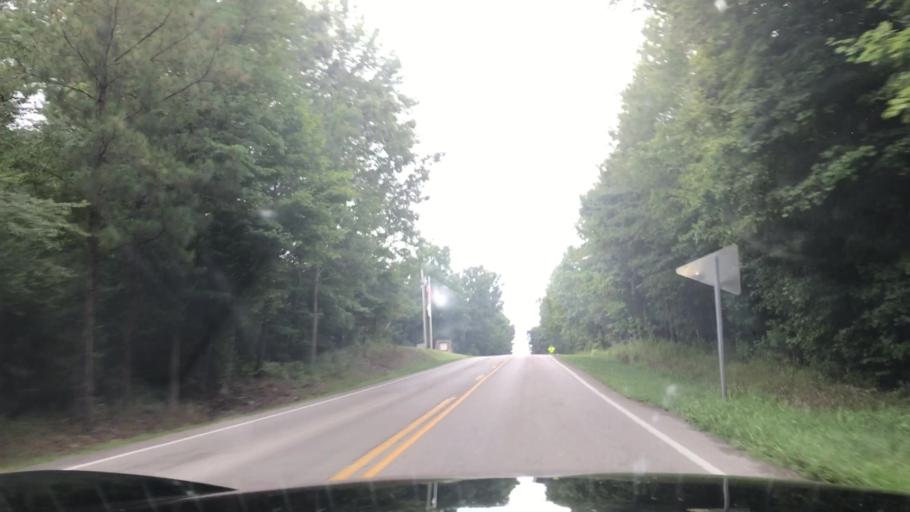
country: US
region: Kentucky
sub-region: Butler County
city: Morgantown
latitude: 37.1764
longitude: -86.8042
